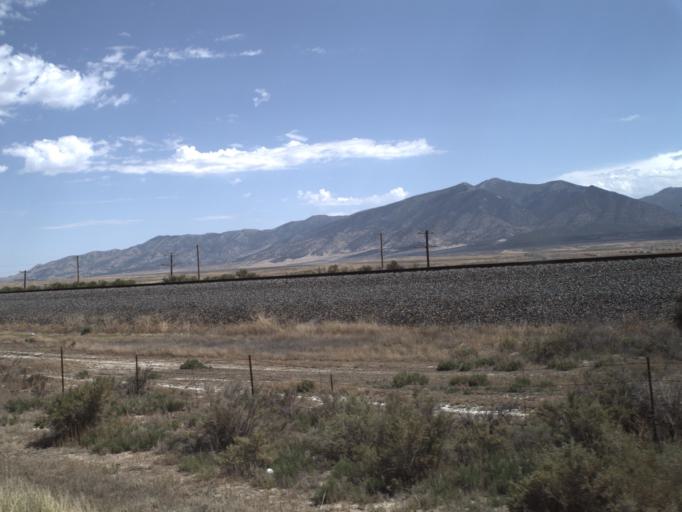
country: US
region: Utah
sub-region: Tooele County
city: Tooele
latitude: 40.2964
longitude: -112.4017
